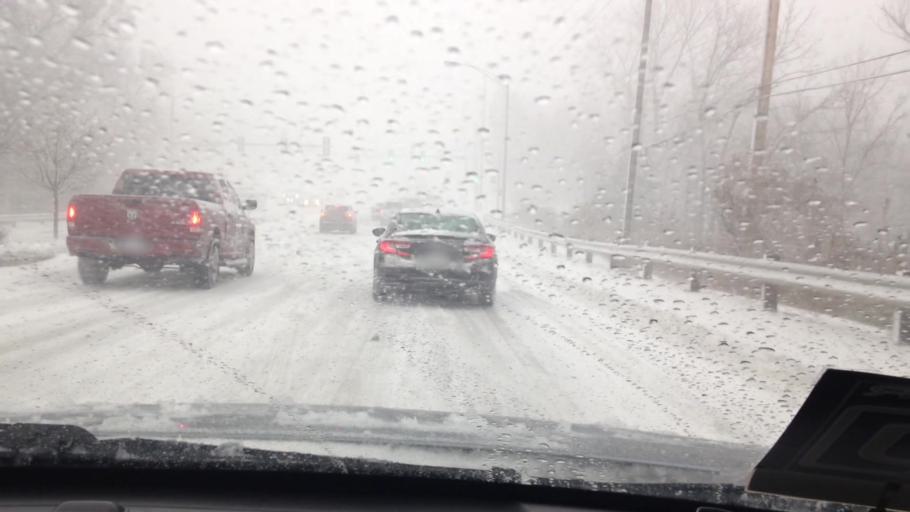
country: US
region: Kansas
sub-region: Johnson County
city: Shawnee
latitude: 39.1166
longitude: -94.7063
